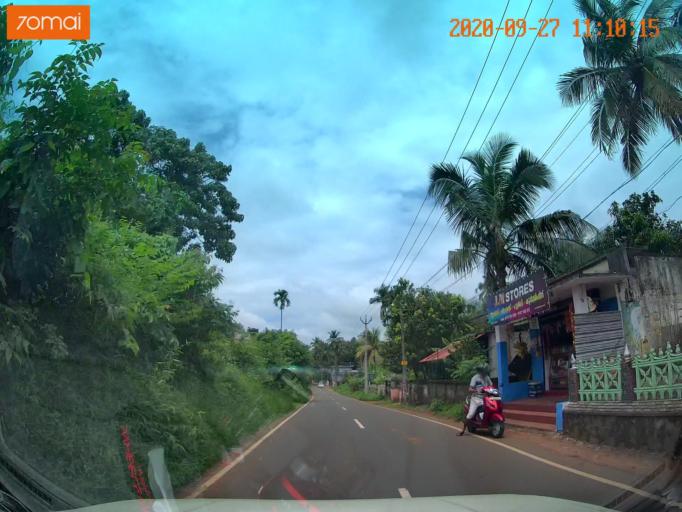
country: IN
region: Kerala
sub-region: Thrissur District
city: Trichur
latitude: 10.4304
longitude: 76.2215
